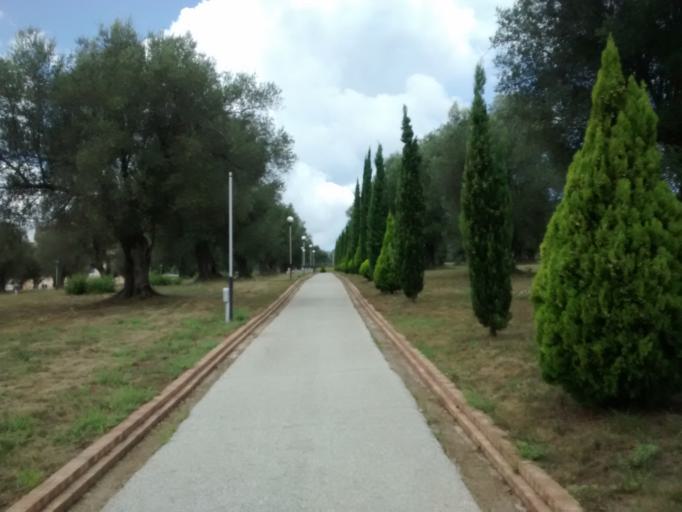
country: IT
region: Calabria
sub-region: Provincia di Vibo-Valentia
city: Vibo Valentia
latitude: 38.6633
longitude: 16.0784
